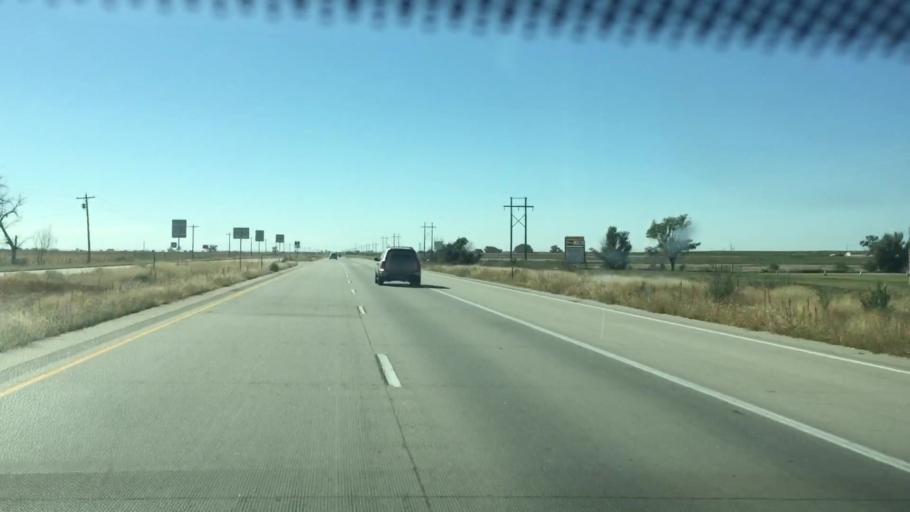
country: US
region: Colorado
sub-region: Prowers County
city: Lamar
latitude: 38.1114
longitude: -102.6601
